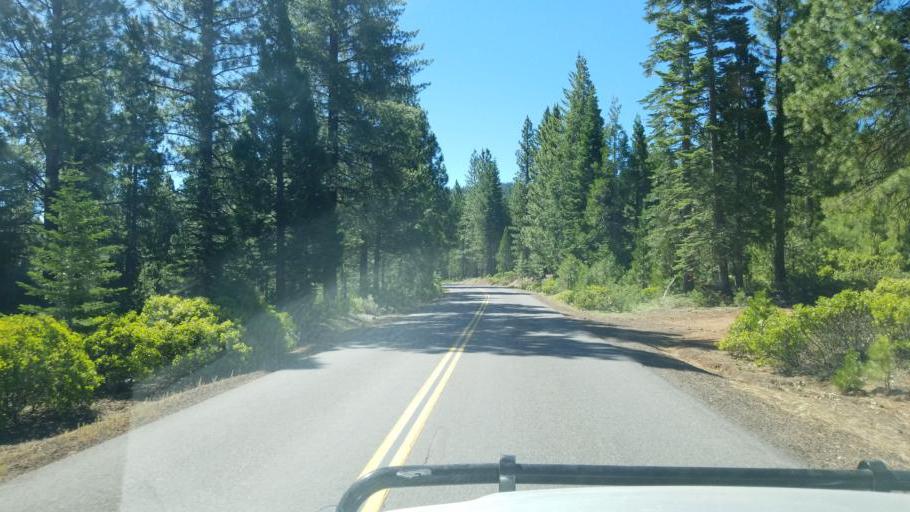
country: US
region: California
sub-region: Lassen County
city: Susanville
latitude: 40.5169
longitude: -120.7832
